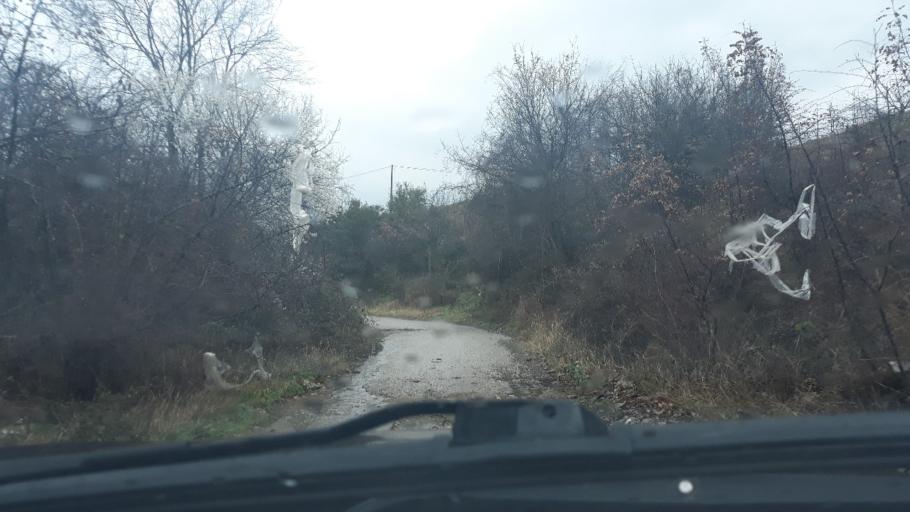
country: MK
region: Valandovo
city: Valandovo
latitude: 41.3186
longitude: 22.5456
